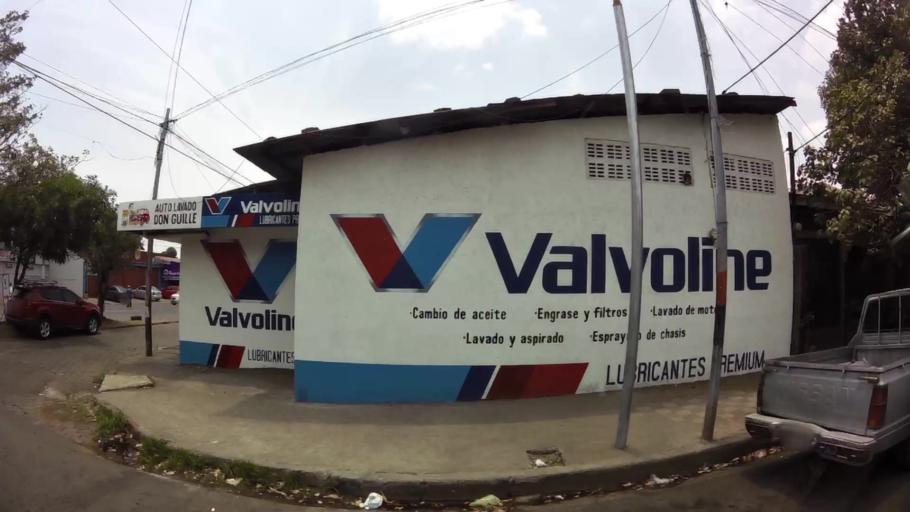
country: NI
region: Managua
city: Managua
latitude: 12.1380
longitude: -86.2925
